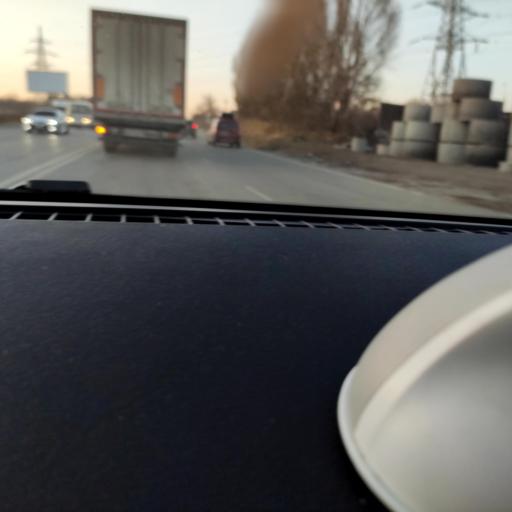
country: RU
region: Samara
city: Petra-Dubrava
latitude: 53.2586
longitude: 50.2936
